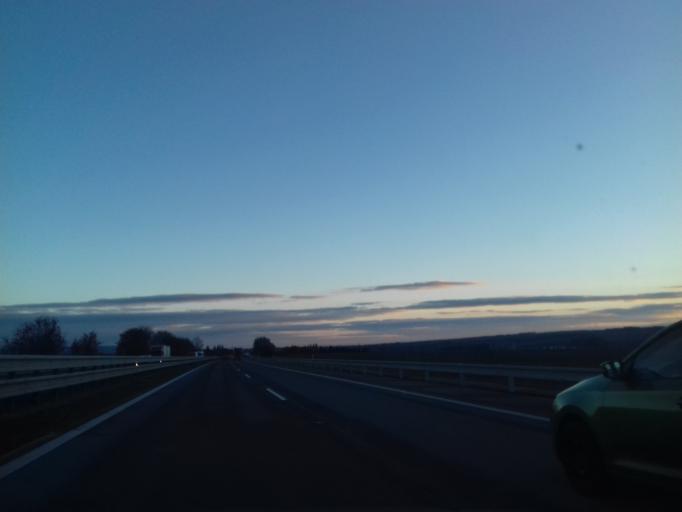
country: CZ
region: South Moravian
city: Drnovice
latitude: 49.2382
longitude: 16.9401
